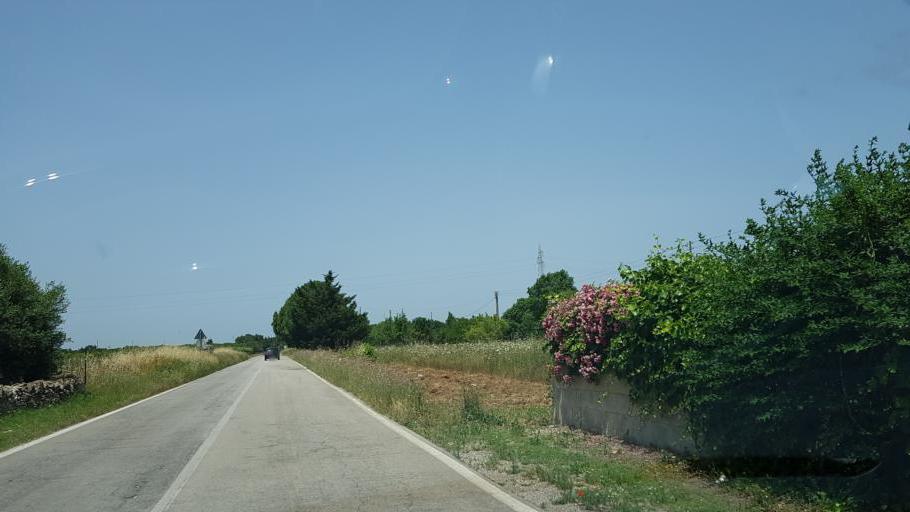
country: IT
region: Apulia
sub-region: Provincia di Brindisi
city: Mesagne
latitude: 40.5349
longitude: 17.8187
